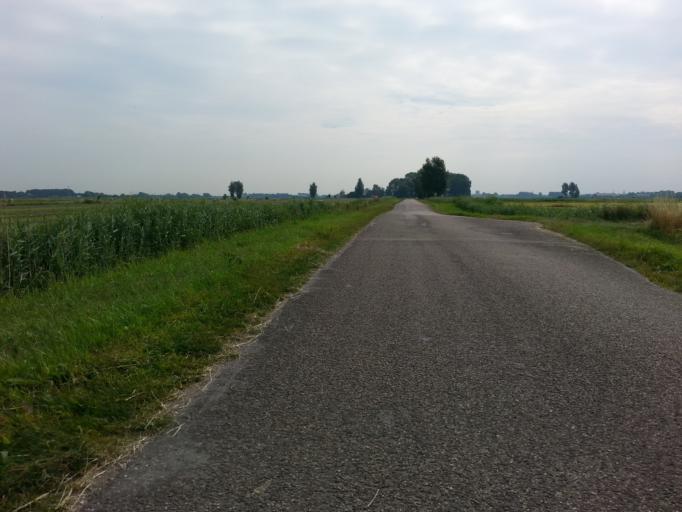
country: NL
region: Utrecht
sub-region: Gemeente Baarn
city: Baarn
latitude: 52.2030
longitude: 5.3219
